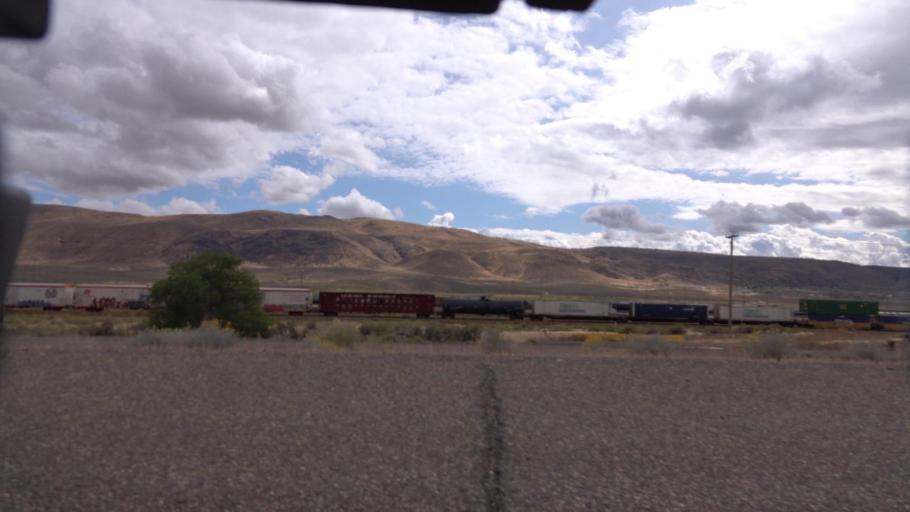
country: US
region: Nevada
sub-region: Elko County
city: Elko
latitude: 40.8810
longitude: -115.7164
